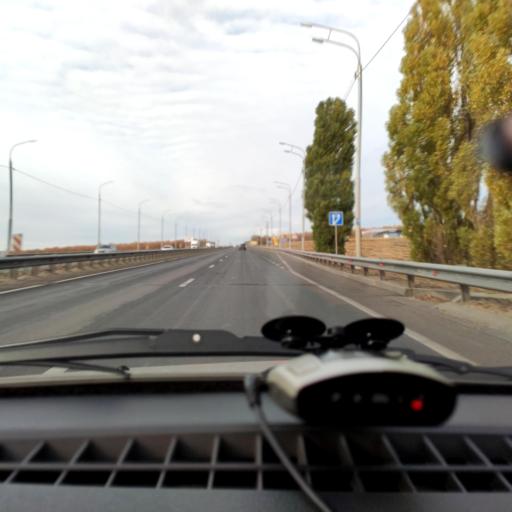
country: RU
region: Voronezj
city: Pridonskoy
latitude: 51.6519
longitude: 39.0562
